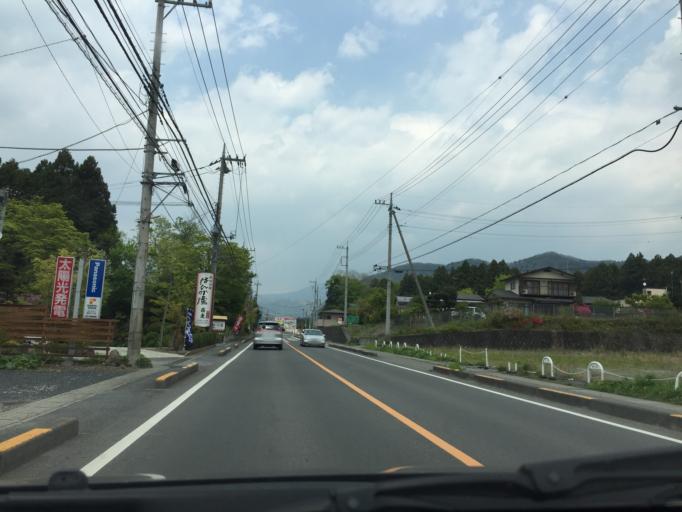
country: JP
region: Tochigi
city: Imaichi
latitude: 36.8105
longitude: 139.7102
